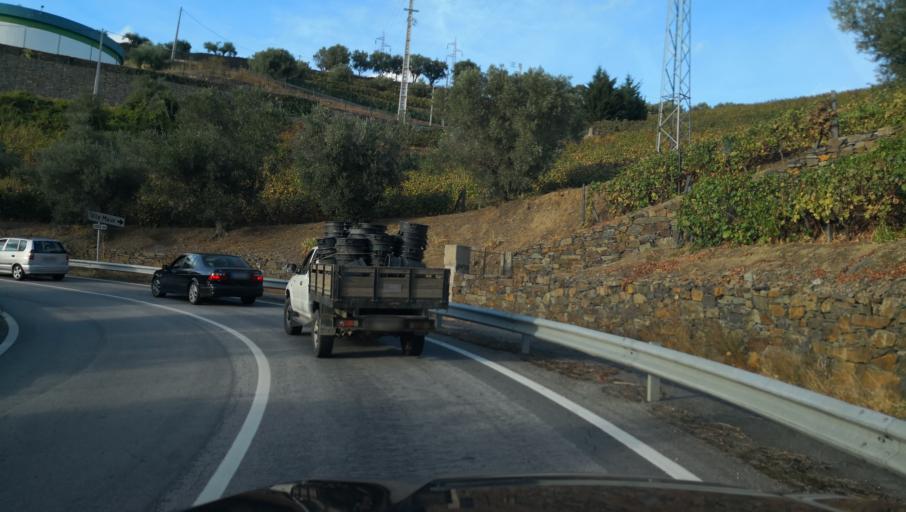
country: PT
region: Vila Real
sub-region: Peso da Regua
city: Peso da Regua
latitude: 41.1745
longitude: -7.7755
